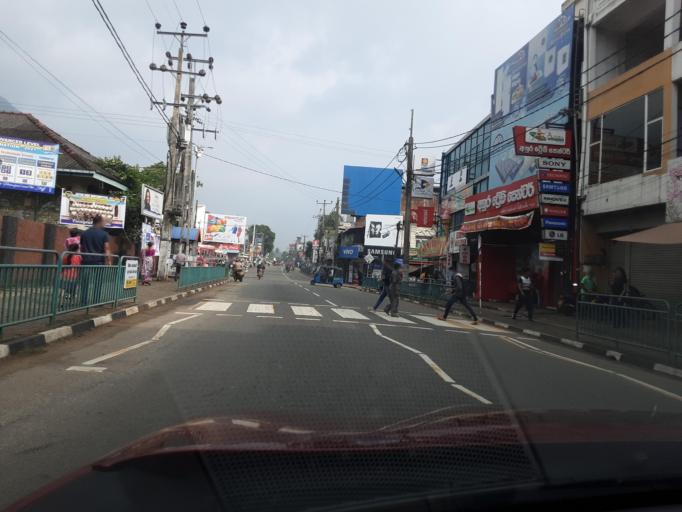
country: LK
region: Central
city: Kandy
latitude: 7.4706
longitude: 80.6227
